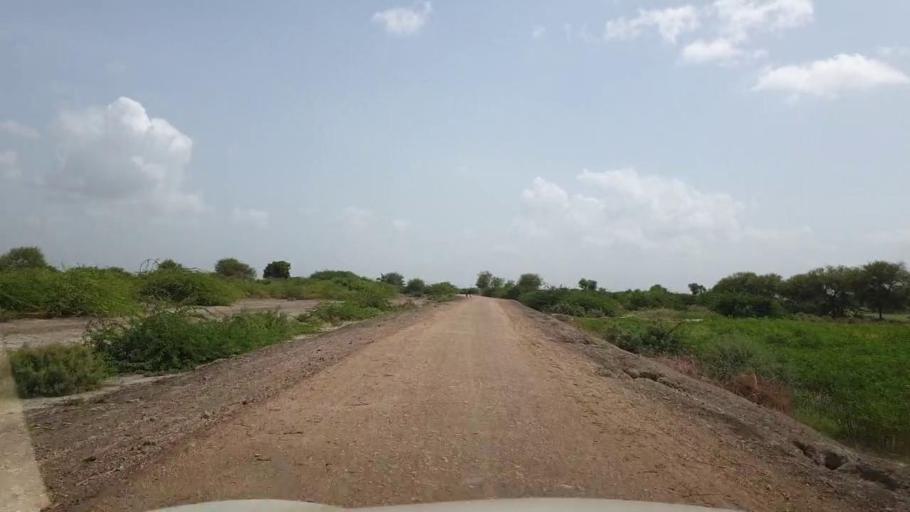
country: PK
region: Sindh
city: Kadhan
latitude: 24.3942
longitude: 68.7952
